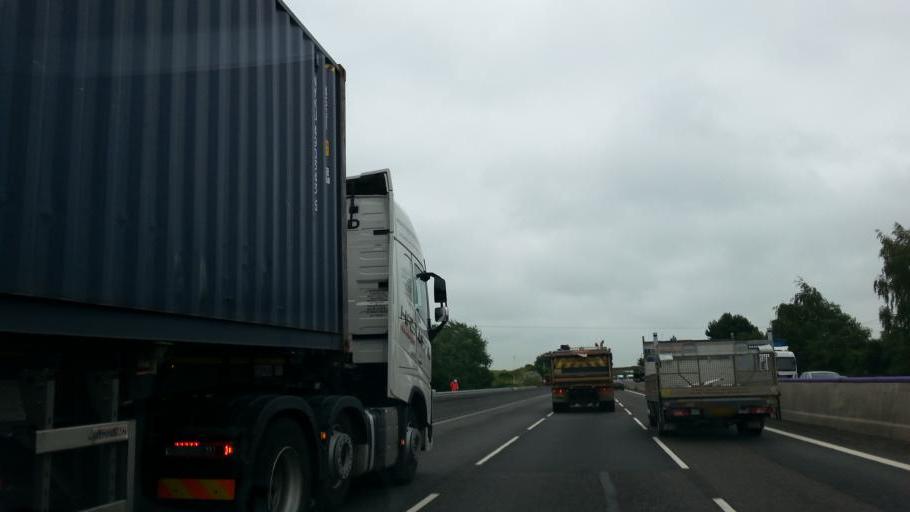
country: GB
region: England
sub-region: Northamptonshire
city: Long Buckby
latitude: 52.2939
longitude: -1.1105
